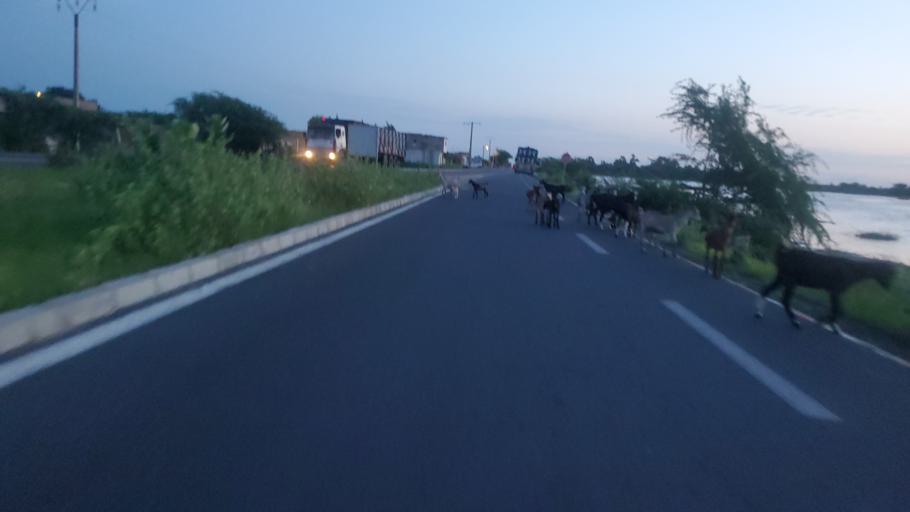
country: SN
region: Saint-Louis
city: Saint-Louis
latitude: 16.0712
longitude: -16.3897
